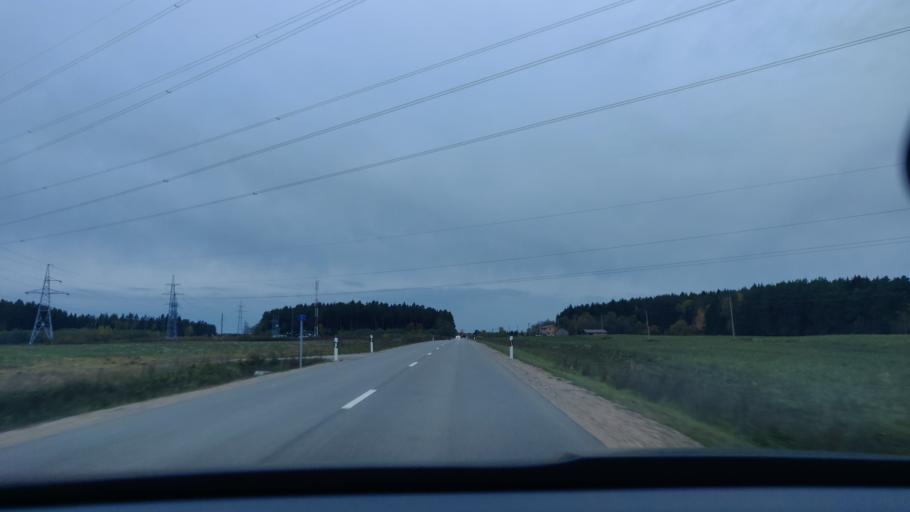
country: LT
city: Lentvaris
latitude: 54.5963
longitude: 25.0335
